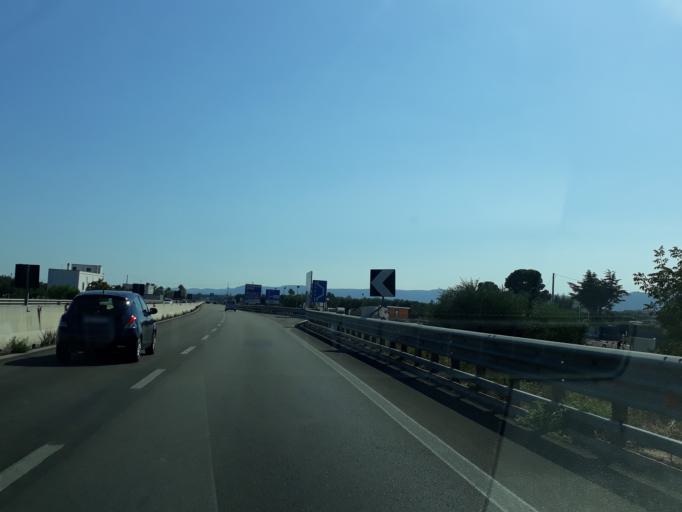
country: IT
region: Apulia
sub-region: Provincia di Brindisi
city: Fasano
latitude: 40.8573
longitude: 17.3506
